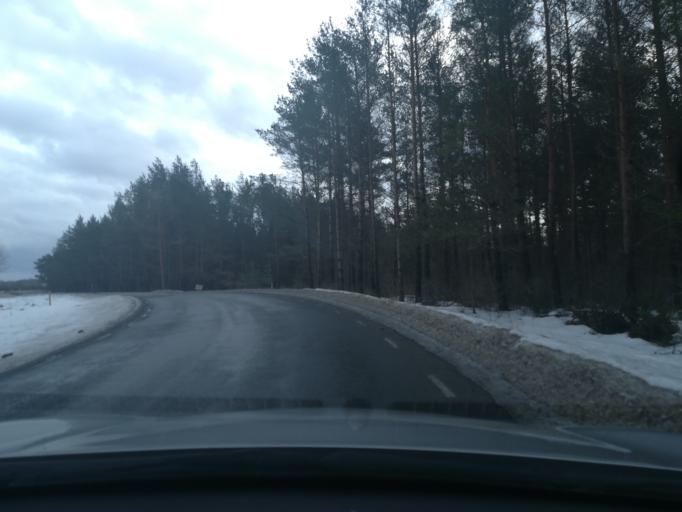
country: EE
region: Harju
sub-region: Saue linn
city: Saue
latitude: 59.3629
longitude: 24.5181
